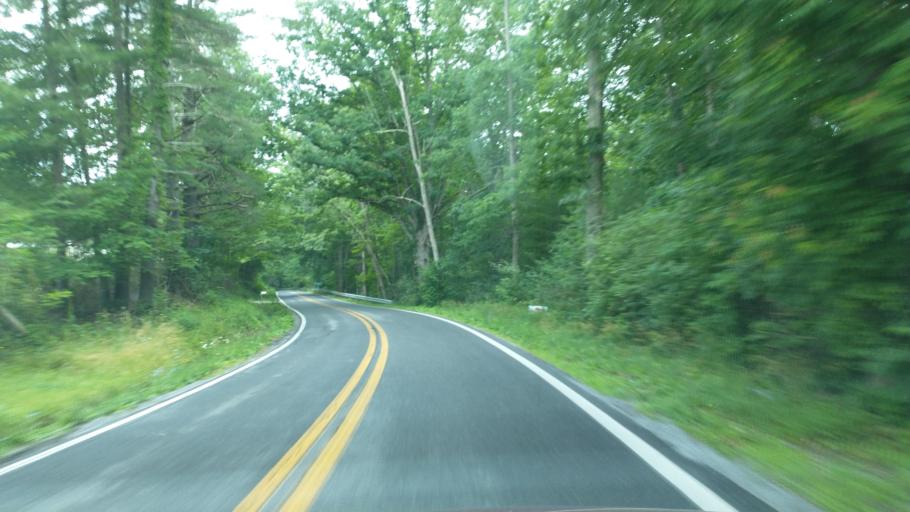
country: US
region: West Virginia
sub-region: Mercer County
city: Athens
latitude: 37.4162
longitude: -81.0455
